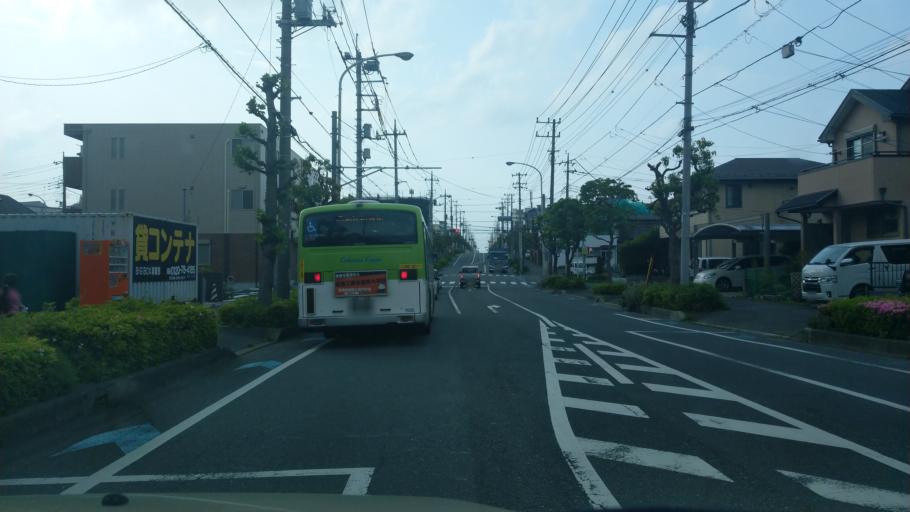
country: JP
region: Saitama
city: Saitama
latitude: 35.8815
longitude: 139.6900
